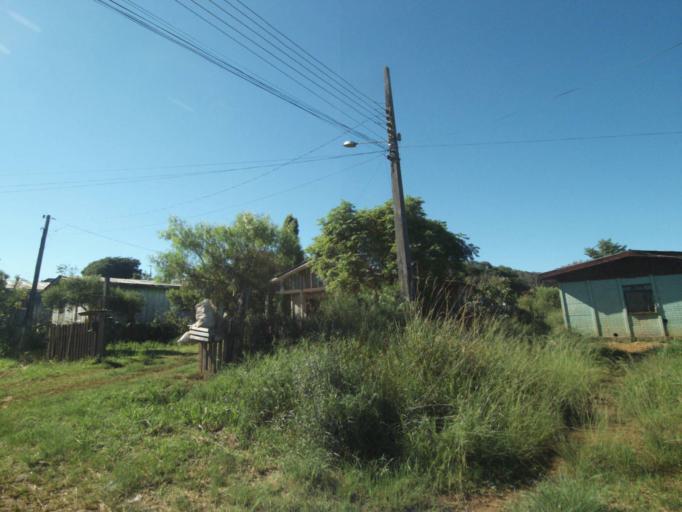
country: BR
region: Parana
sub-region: Pinhao
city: Pinhao
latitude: -25.8444
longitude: -52.0327
